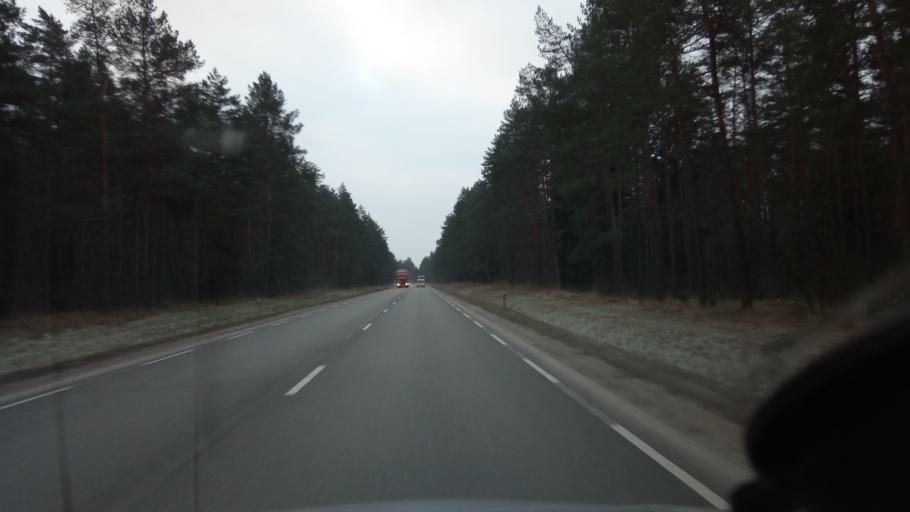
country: LT
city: Trakai
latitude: 54.5175
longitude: 24.9838
